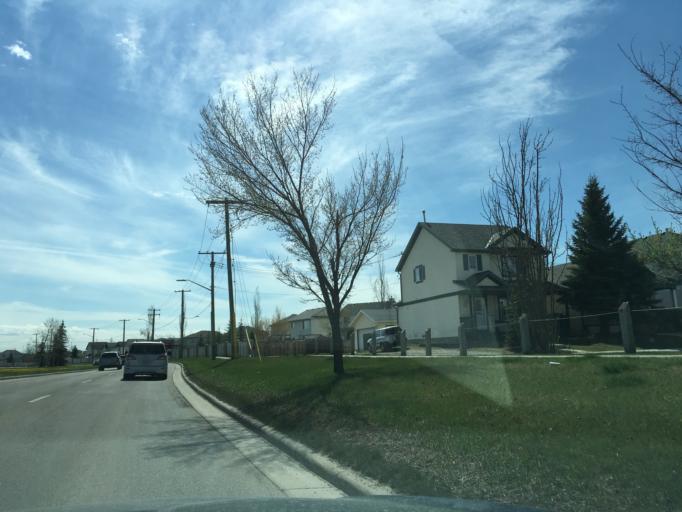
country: CA
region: Alberta
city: Calgary
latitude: 50.9061
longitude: -114.1034
